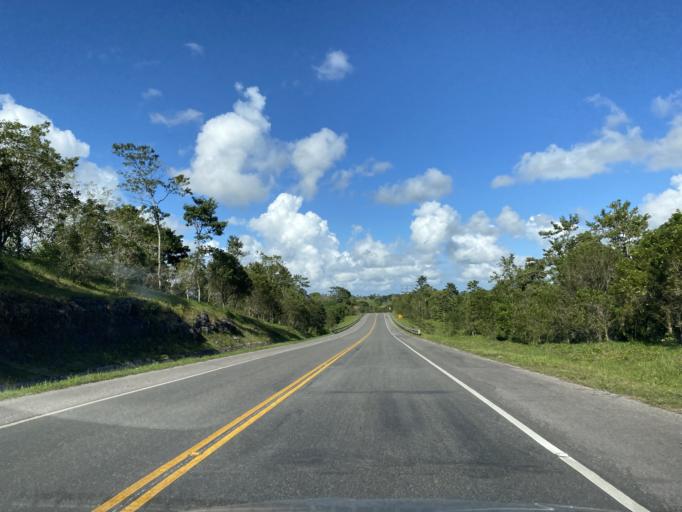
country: DO
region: Monte Plata
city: Majagual
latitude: 19.0193
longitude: -69.8227
